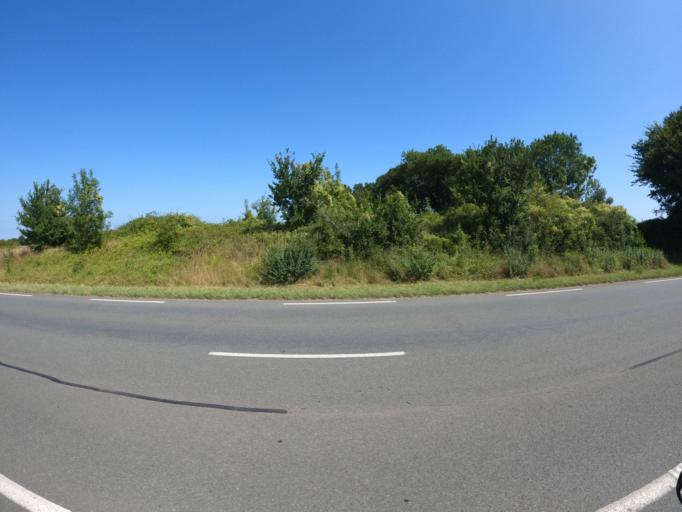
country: FR
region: Poitou-Charentes
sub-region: Departement des Deux-Sevres
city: Thorigne
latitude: 46.2816
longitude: -0.2566
